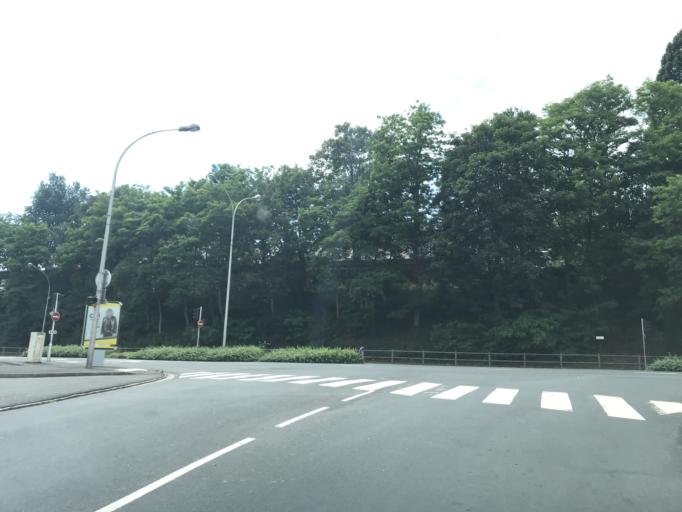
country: FR
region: Haute-Normandie
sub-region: Departement de la Seine-Maritime
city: Mont-Saint-Aignan
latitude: 49.4585
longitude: 1.0834
